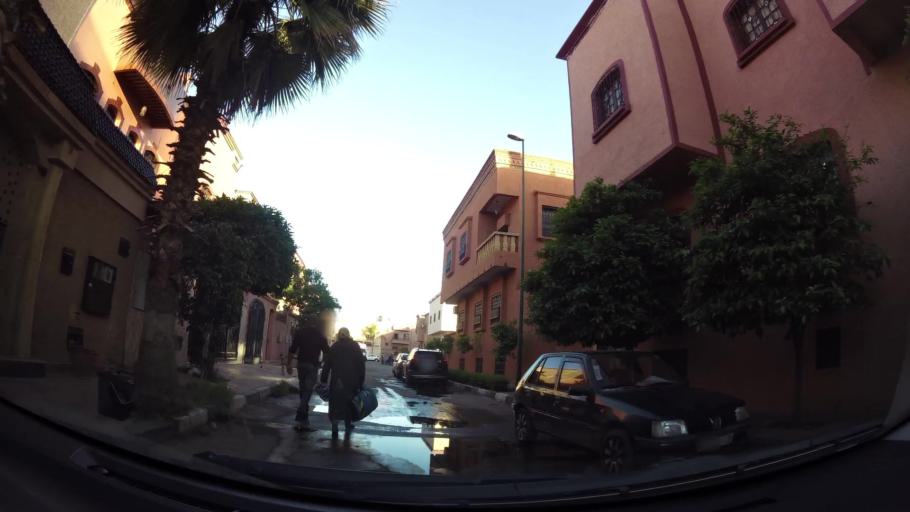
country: MA
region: Marrakech-Tensift-Al Haouz
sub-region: Marrakech
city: Marrakesh
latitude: 31.6242
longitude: -8.0330
